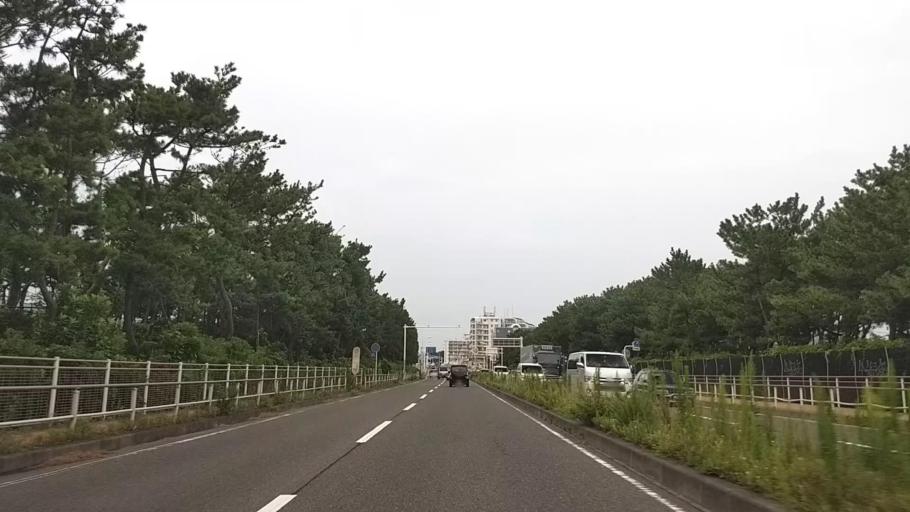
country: JP
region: Kanagawa
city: Chigasaki
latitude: 35.3187
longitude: 139.4043
